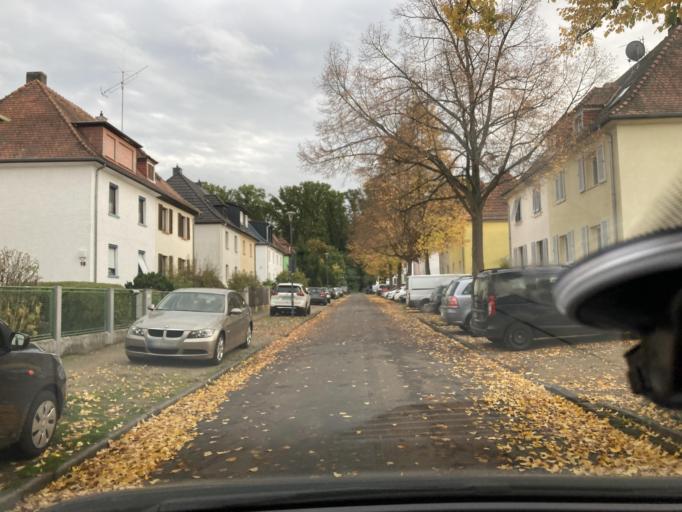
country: DE
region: Hesse
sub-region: Regierungsbezirk Darmstadt
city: Offenbach
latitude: 50.0826
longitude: 8.7797
